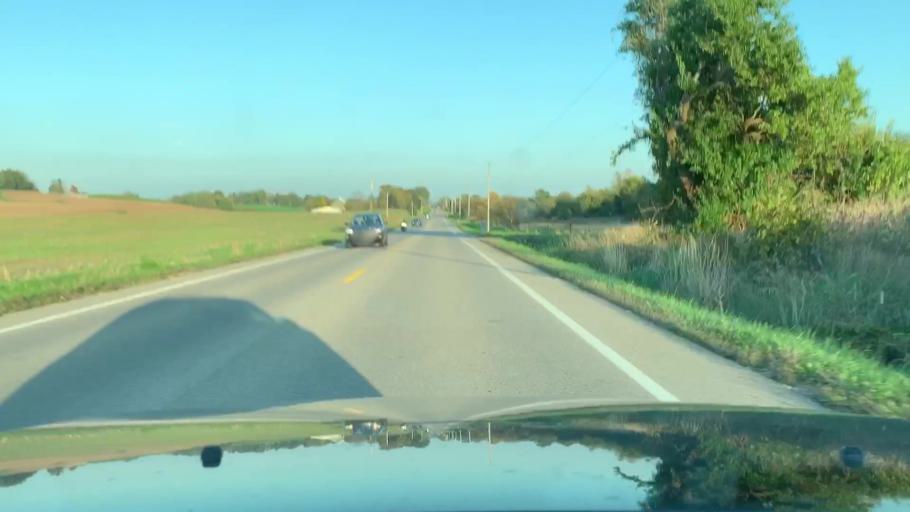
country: US
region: Michigan
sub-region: Ottawa County
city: Hudsonville
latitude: 42.8115
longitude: -85.8128
